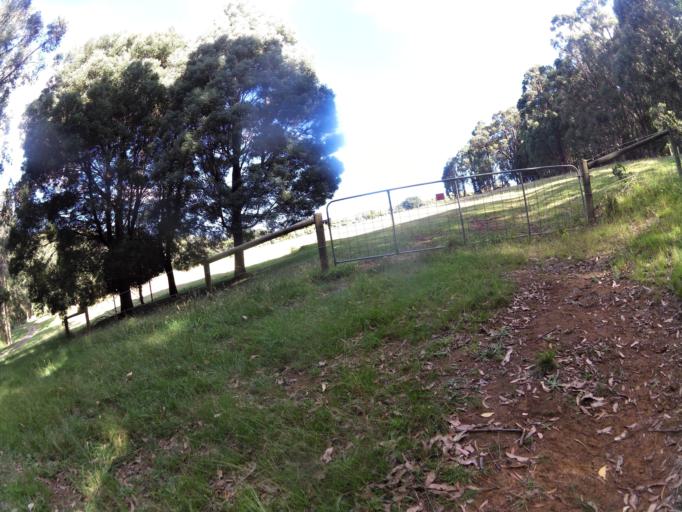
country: AU
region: Victoria
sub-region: Yarra Ranges
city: Ferny Creek
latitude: -37.8742
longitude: 145.3378
